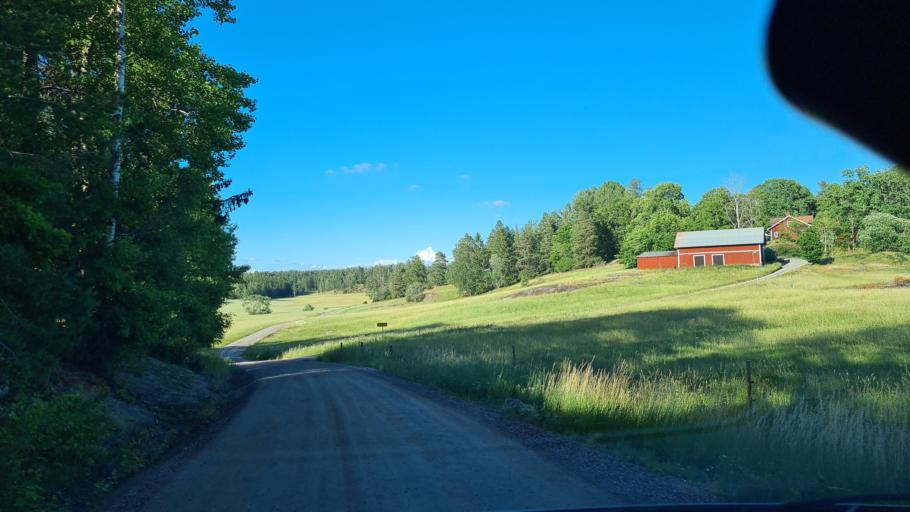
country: SE
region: Soedermanland
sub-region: Nykopings Kommun
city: Nykoping
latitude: 58.9209
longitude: 17.0466
